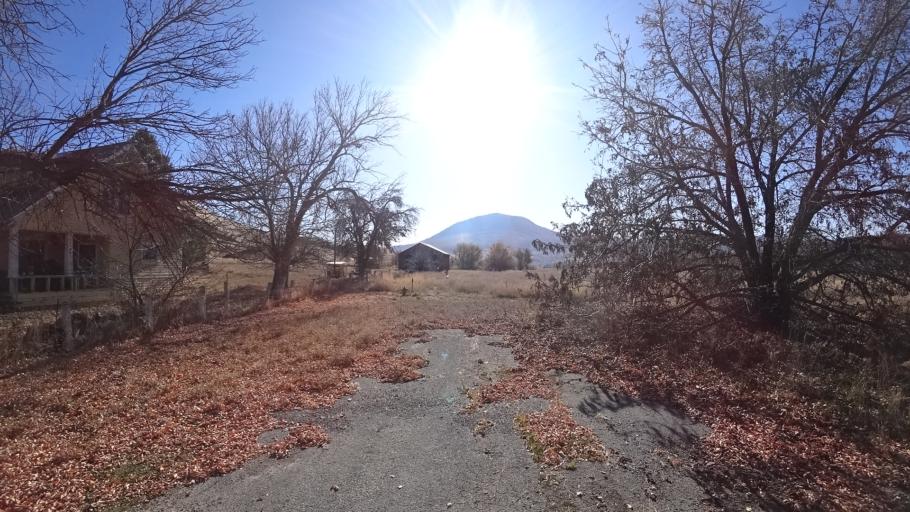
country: US
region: California
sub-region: Siskiyou County
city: Montague
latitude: 41.9081
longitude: -122.5521
